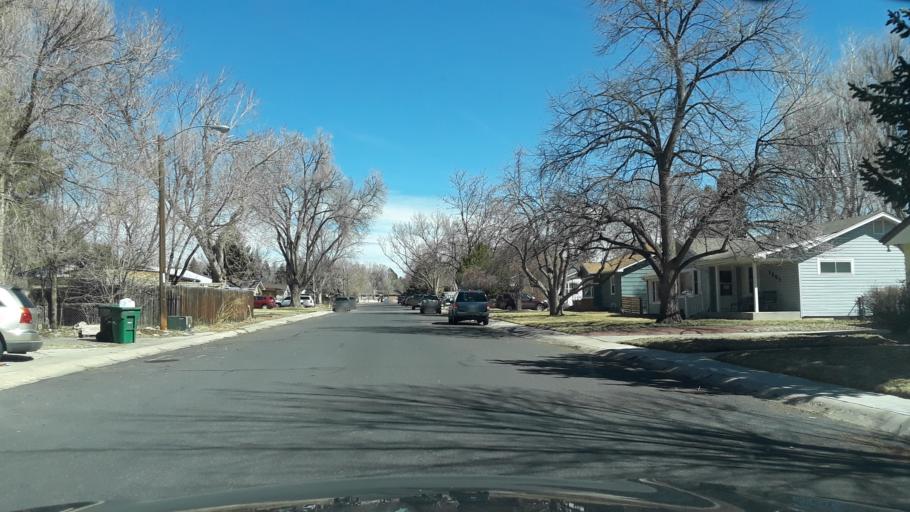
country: US
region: Colorado
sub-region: El Paso County
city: Colorado Springs
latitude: 38.8717
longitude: -104.8031
